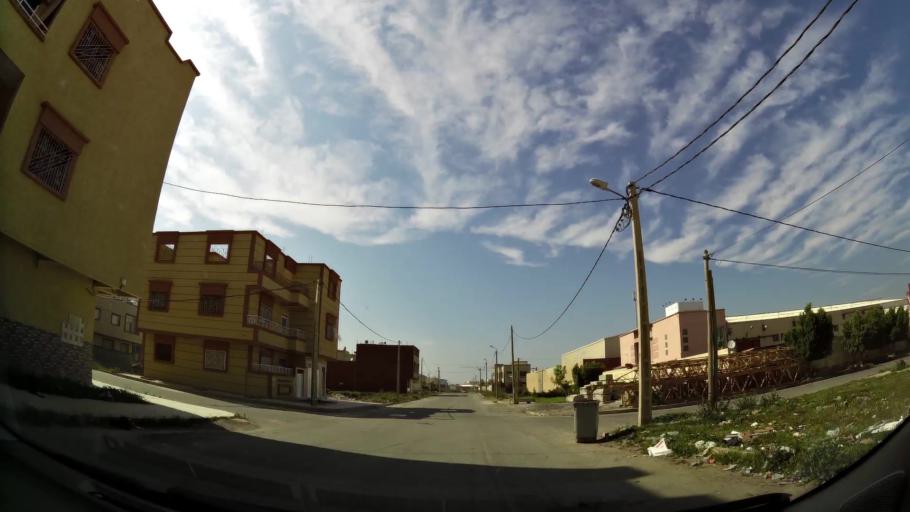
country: MA
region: Oriental
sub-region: Oujda-Angad
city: Oujda
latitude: 34.7007
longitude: -1.8843
